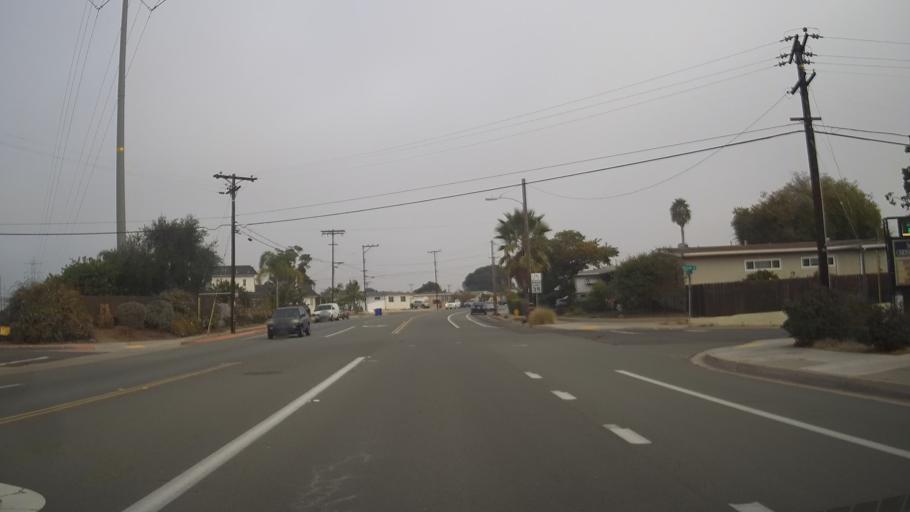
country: US
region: California
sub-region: San Diego County
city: San Diego
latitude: 32.7934
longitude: -117.1445
